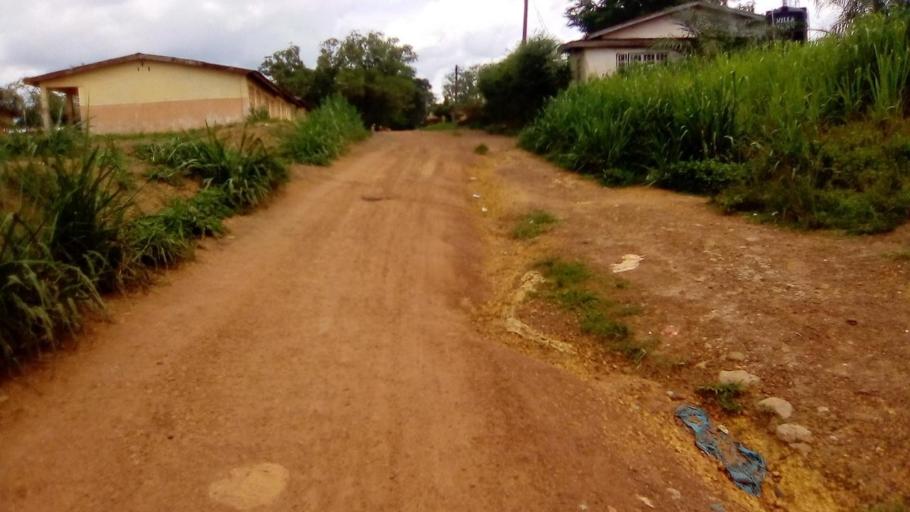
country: SL
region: Southern Province
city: Bo
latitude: 7.9584
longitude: -11.7289
